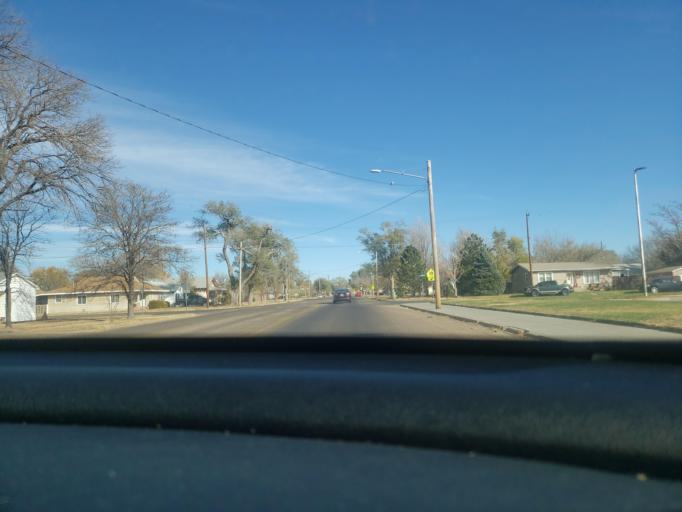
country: US
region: Kansas
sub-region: Finney County
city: Garden City
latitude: 37.9790
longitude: -100.8703
